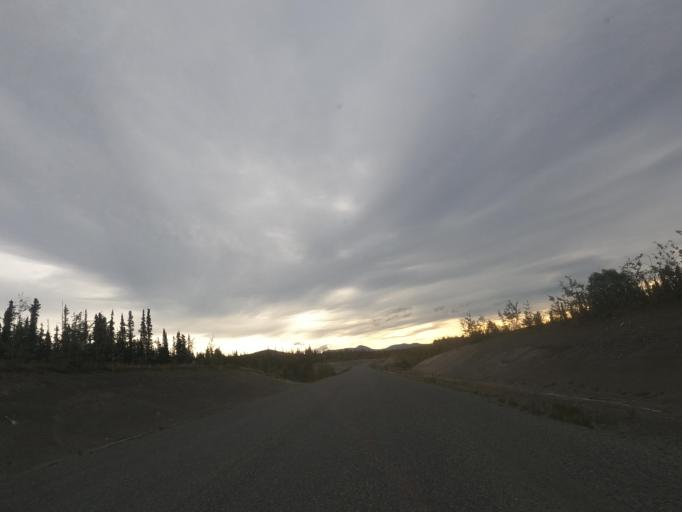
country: CA
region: Yukon
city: Haines Junction
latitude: 60.8143
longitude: -136.6779
